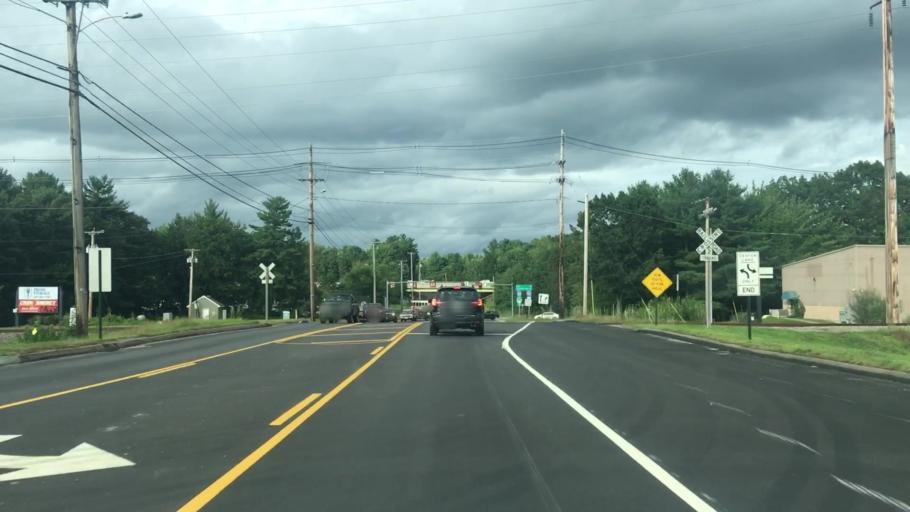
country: US
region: Maine
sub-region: York County
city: Saco
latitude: 43.5211
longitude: -70.4481
